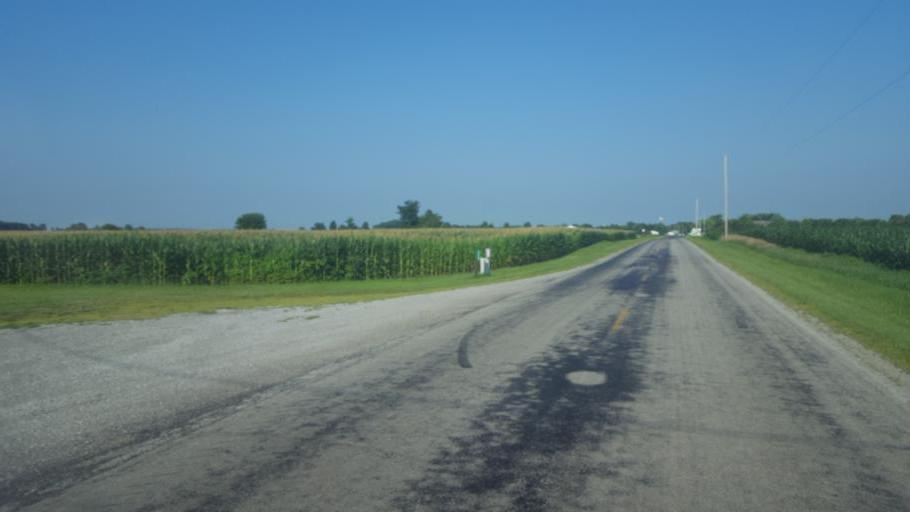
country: US
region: Ohio
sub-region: Hardin County
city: Kenton
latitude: 40.5346
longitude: -83.5049
